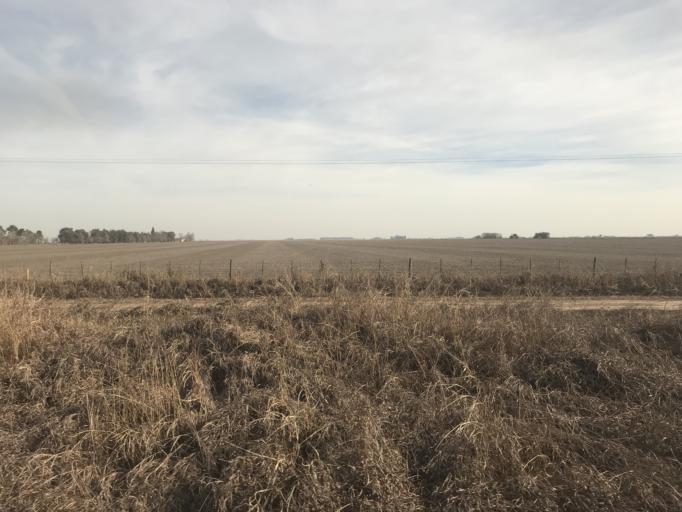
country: AR
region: Cordoba
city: Pilar
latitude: -31.7082
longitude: -63.8631
